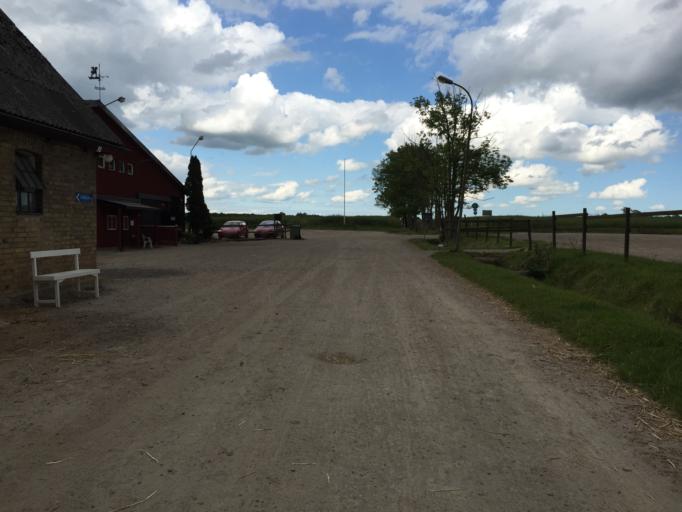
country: SE
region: Skane
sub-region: Lunds Kommun
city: Lund
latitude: 55.7410
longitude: 13.1842
